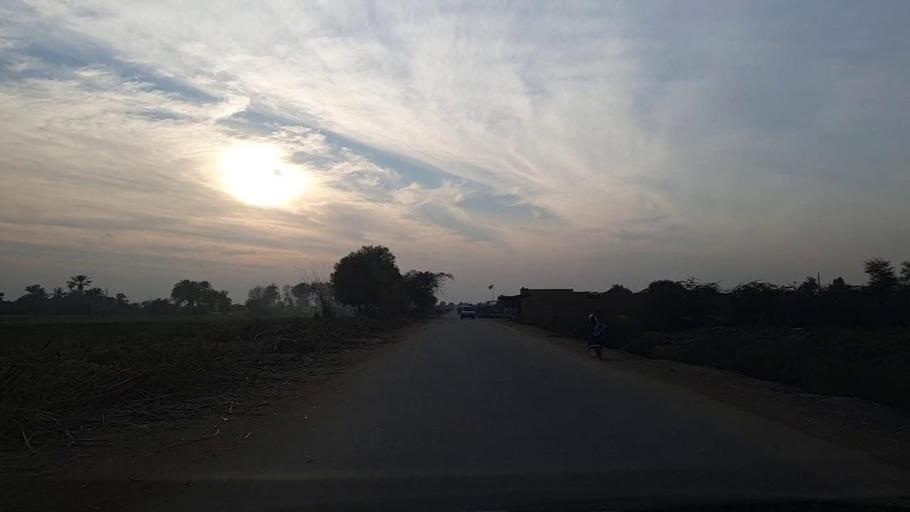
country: PK
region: Sindh
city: Daur
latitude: 26.4006
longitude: 68.4672
